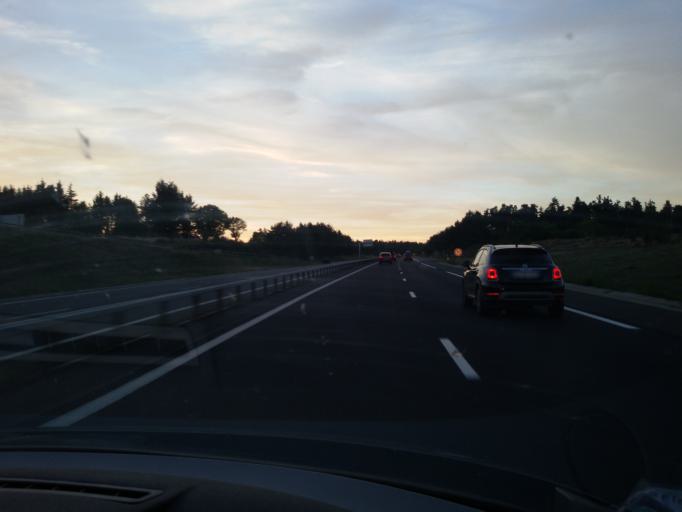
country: FR
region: Languedoc-Roussillon
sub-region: Departement de la Lozere
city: Le Malzieu-Ville
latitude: 44.8213
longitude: 3.2702
